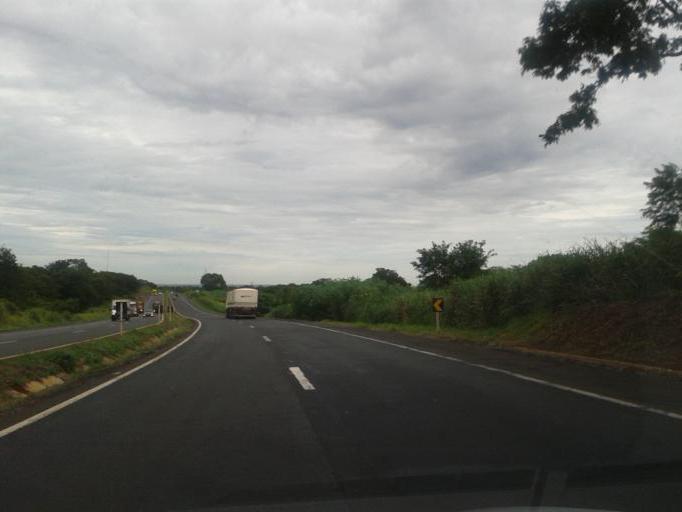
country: BR
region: Minas Gerais
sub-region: Centralina
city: Centralina
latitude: -18.6247
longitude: -49.1862
